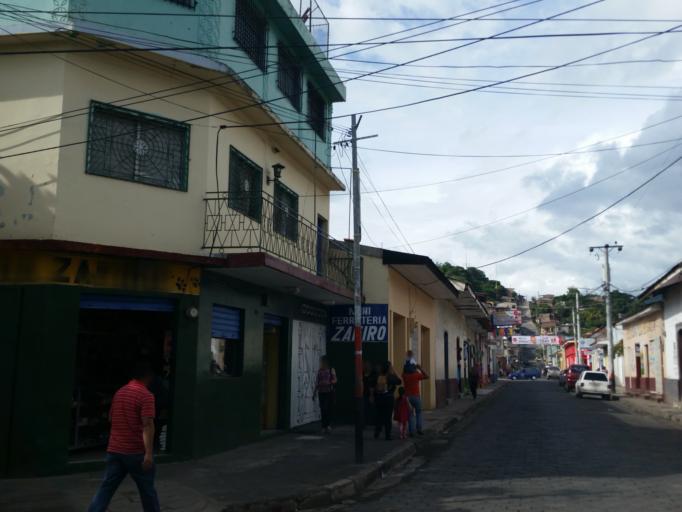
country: NI
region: Matagalpa
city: Matagalpa
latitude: 12.9280
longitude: -85.9161
